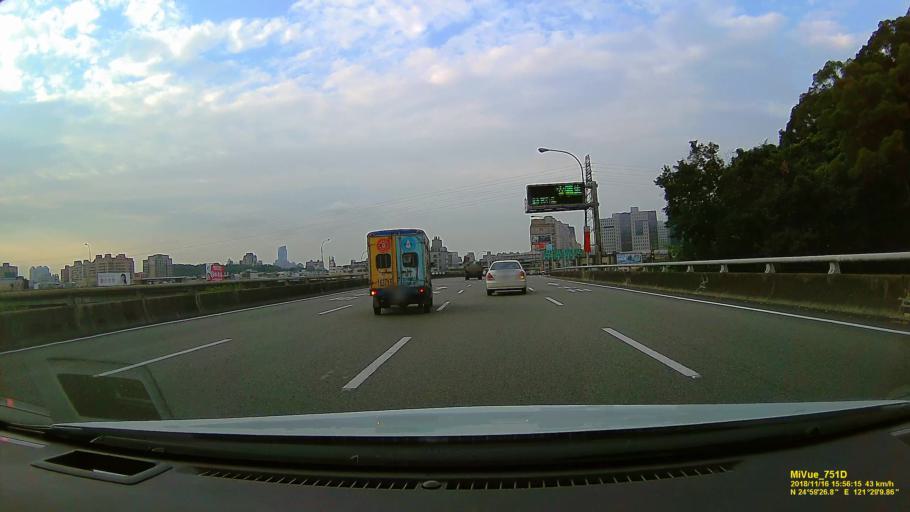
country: TW
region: Taipei
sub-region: Taipei
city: Banqiao
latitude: 24.9904
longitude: 121.4860
